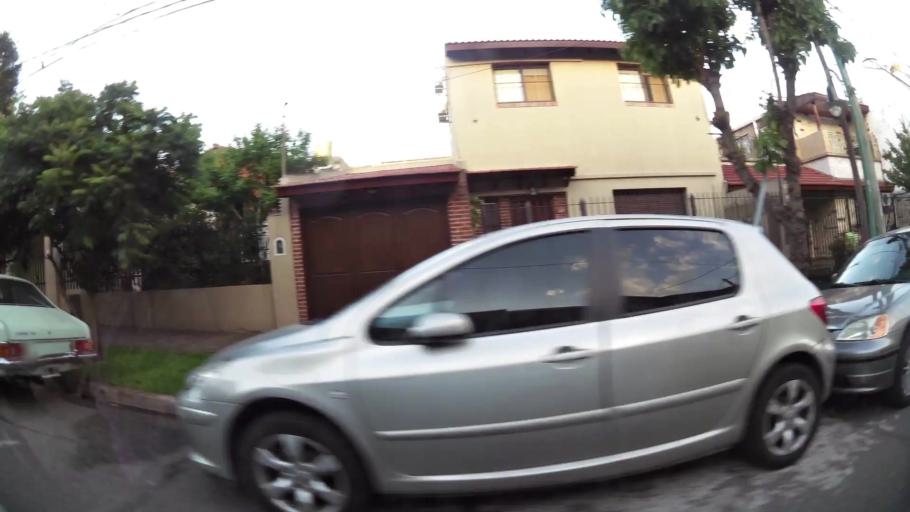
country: AR
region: Buenos Aires
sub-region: Partido de Vicente Lopez
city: Olivos
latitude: -34.5377
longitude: -58.5064
